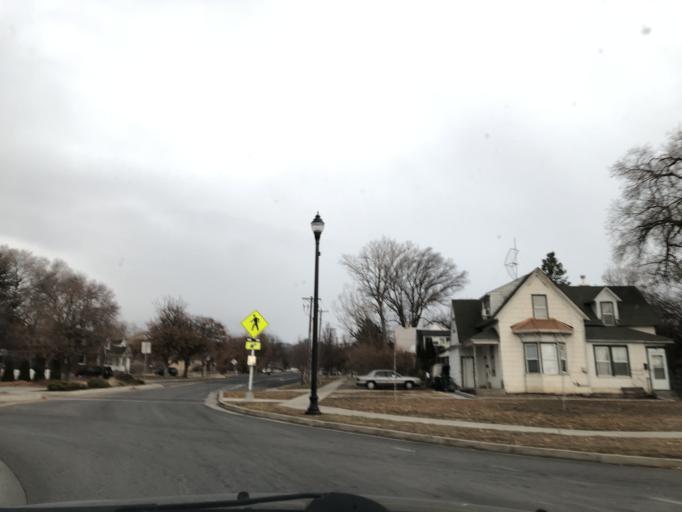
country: US
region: Utah
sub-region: Cache County
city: Logan
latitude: 41.7408
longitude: -111.8295
